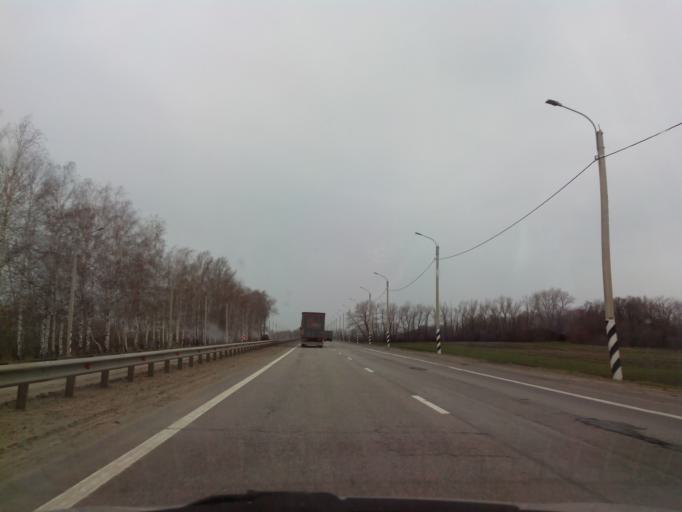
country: RU
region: Tambov
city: Selezni
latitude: 52.7485
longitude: 41.1881
